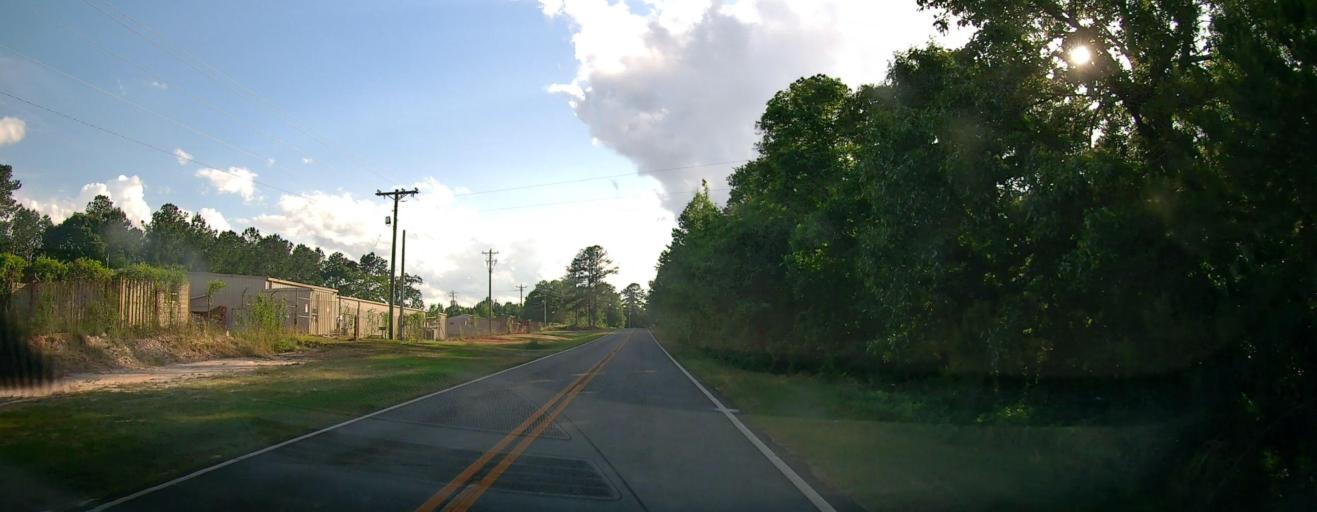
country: US
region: Georgia
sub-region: Peach County
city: Byron
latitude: 32.6727
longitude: -83.7886
